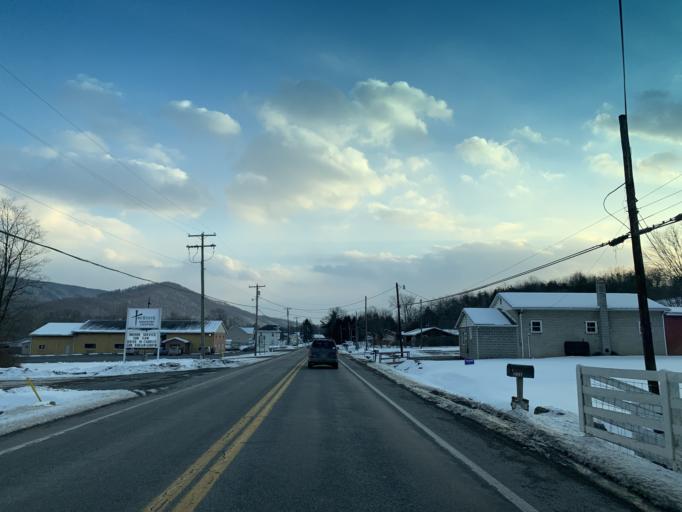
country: US
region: Maryland
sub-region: Allegany County
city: Cumberland
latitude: 39.7269
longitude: -78.7732
